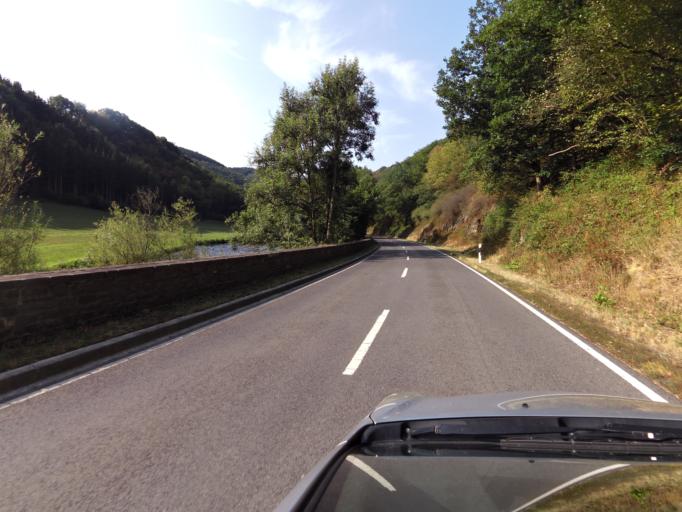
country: LU
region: Diekirch
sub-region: Canton de Diekirch
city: Bourscheid
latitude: 49.9262
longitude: 6.0660
